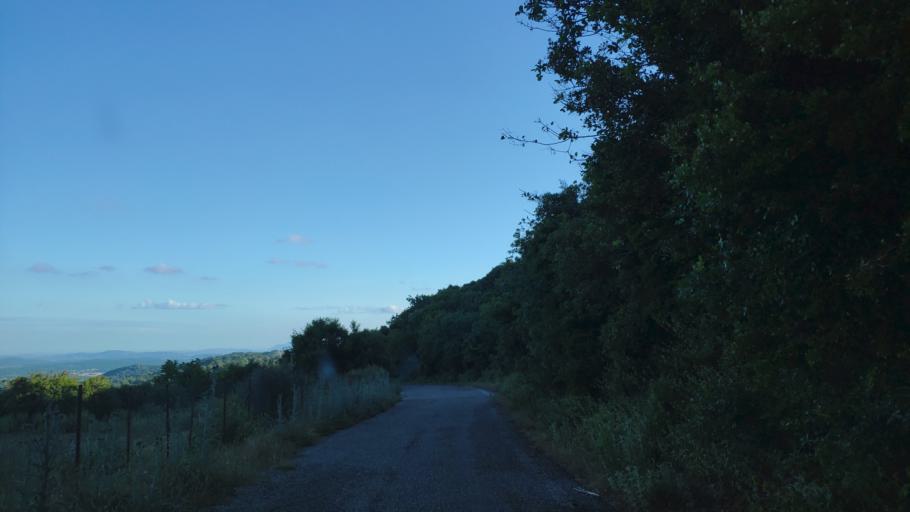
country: GR
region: West Greece
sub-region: Nomos Aitolias kai Akarnanias
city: Fitiai
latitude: 38.6485
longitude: 21.1985
